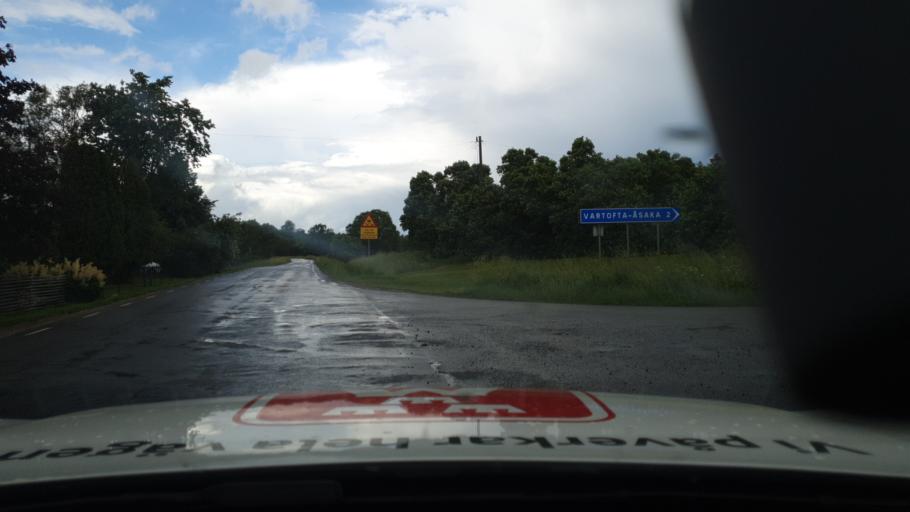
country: SE
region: Vaestra Goetaland
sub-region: Falkopings Kommun
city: Falkoeping
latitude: 58.0747
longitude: 13.6372
